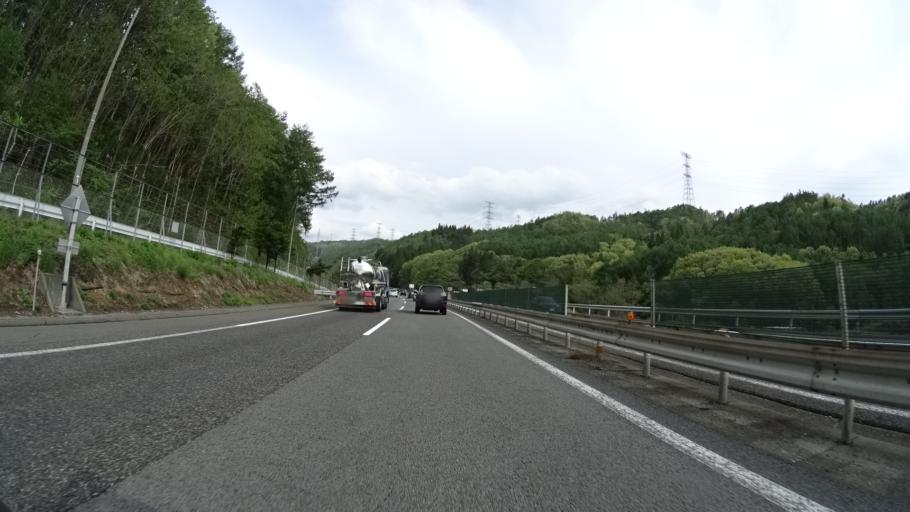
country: JP
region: Nagano
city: Shiojiri
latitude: 36.0909
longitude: 138.0040
